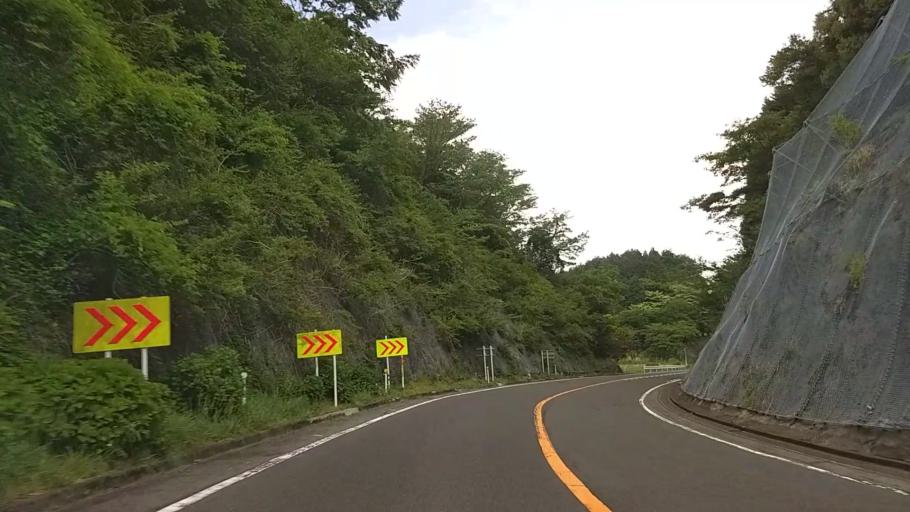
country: JP
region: Kanagawa
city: Odawara
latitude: 35.2147
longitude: 139.1064
